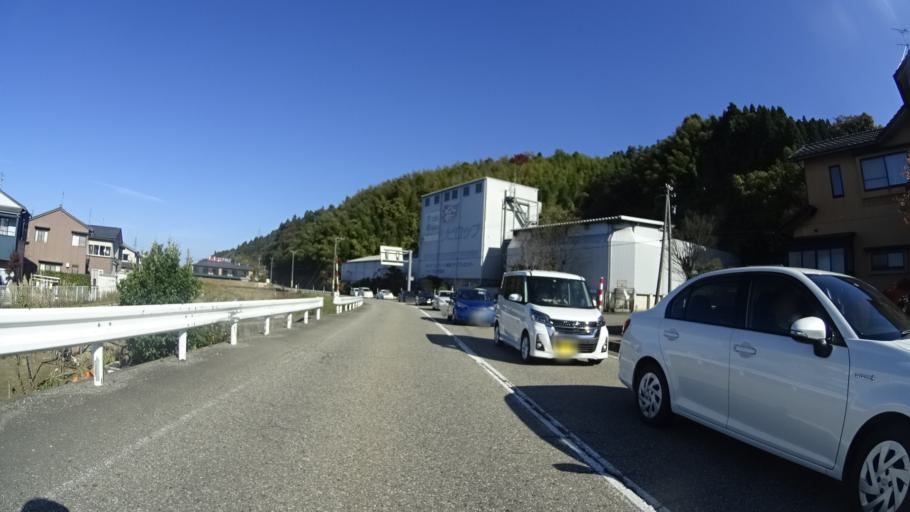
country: JP
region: Ishikawa
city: Tsurugi-asahimachi
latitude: 36.4744
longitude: 136.6161
